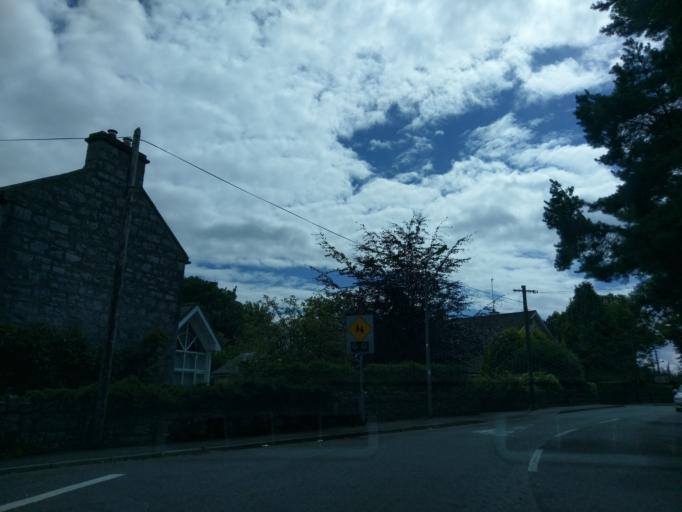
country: IE
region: Connaught
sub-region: County Galway
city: Oranmore
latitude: 53.2647
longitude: -8.9297
